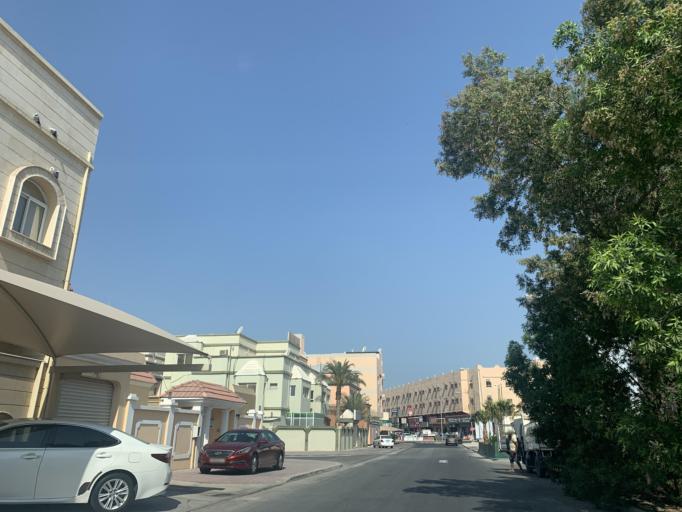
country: BH
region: Central Governorate
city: Madinat Hamad
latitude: 26.1393
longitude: 50.4973
